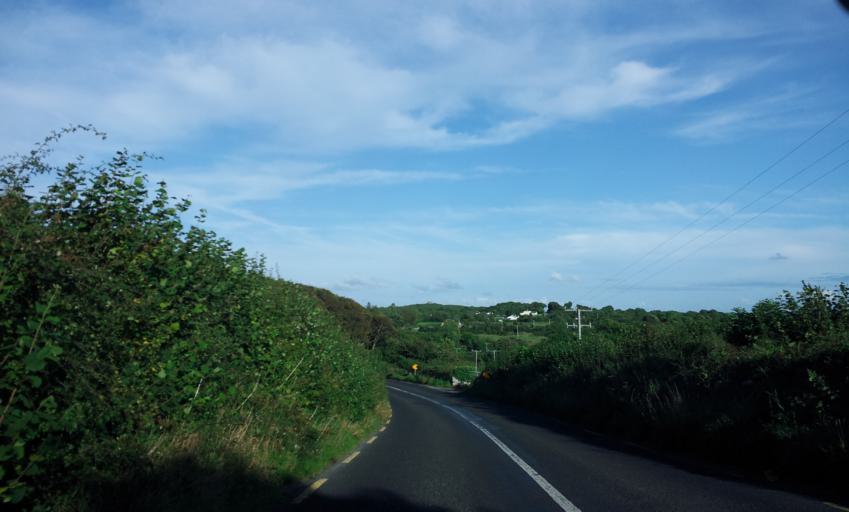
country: IE
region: Munster
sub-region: An Clar
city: Ennis
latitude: 52.9771
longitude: -9.1099
